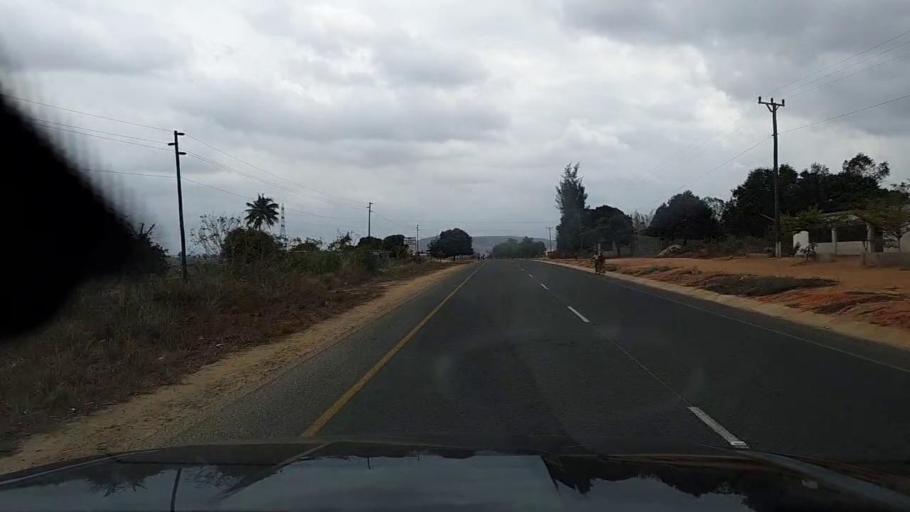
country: MZ
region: Nampula
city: Nampula
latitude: -15.1693
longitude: 39.3078
